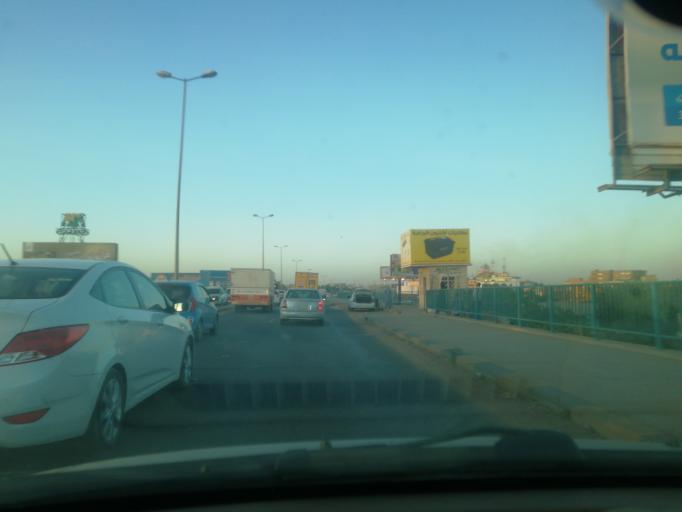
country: SD
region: Khartoum
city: Khartoum
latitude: 15.6197
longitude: 32.5549
